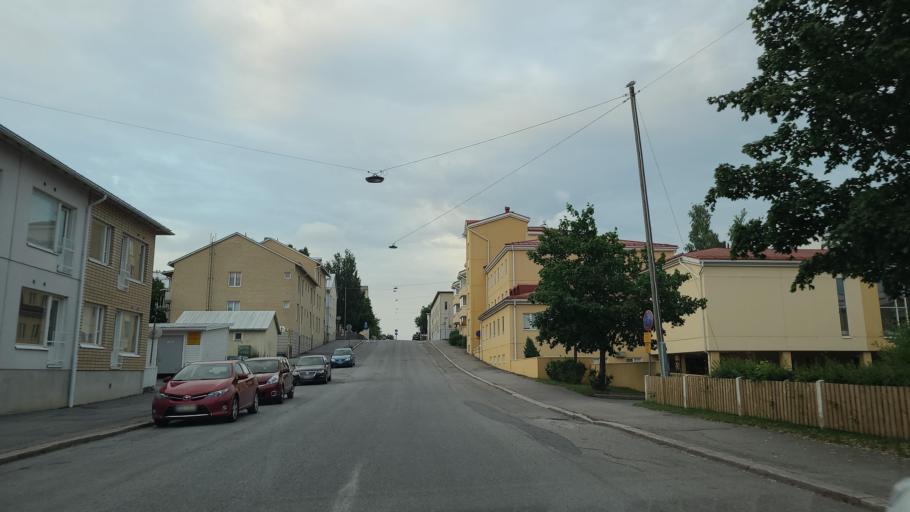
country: FI
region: Ostrobothnia
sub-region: Vaasa
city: Vaasa
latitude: 63.1000
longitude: 21.6161
